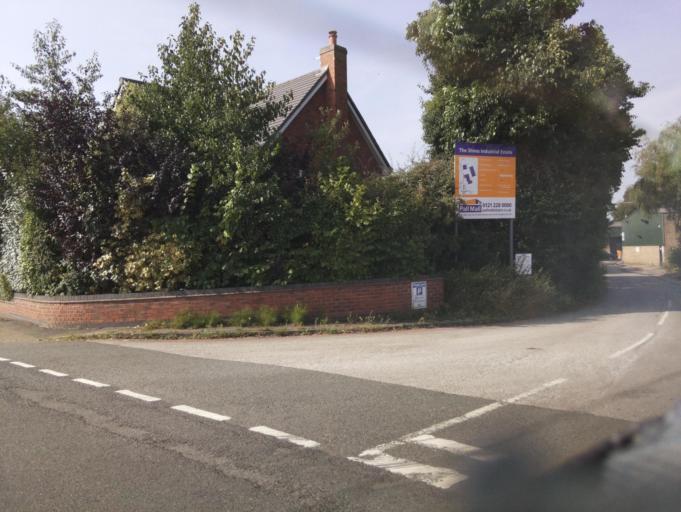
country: GB
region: England
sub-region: Staffordshire
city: Lichfield
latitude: 52.6733
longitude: -1.8316
